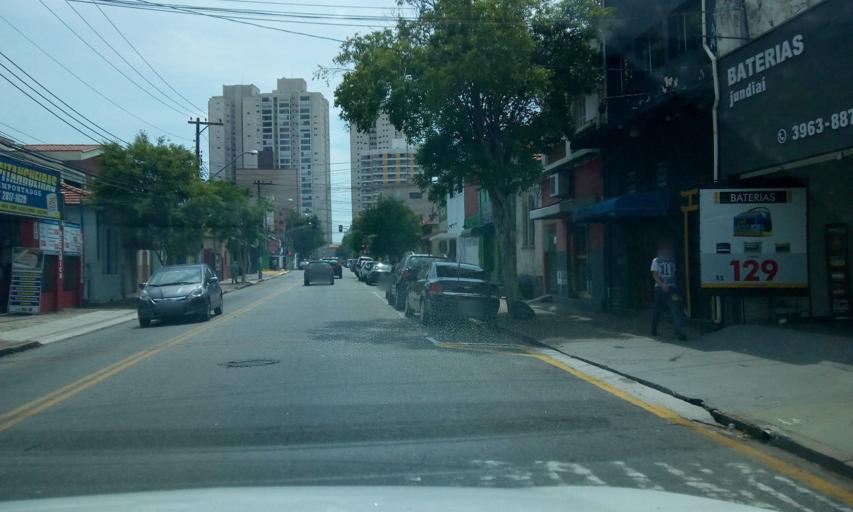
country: BR
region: Sao Paulo
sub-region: Jundiai
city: Jundiai
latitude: -23.2001
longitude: -46.8811
